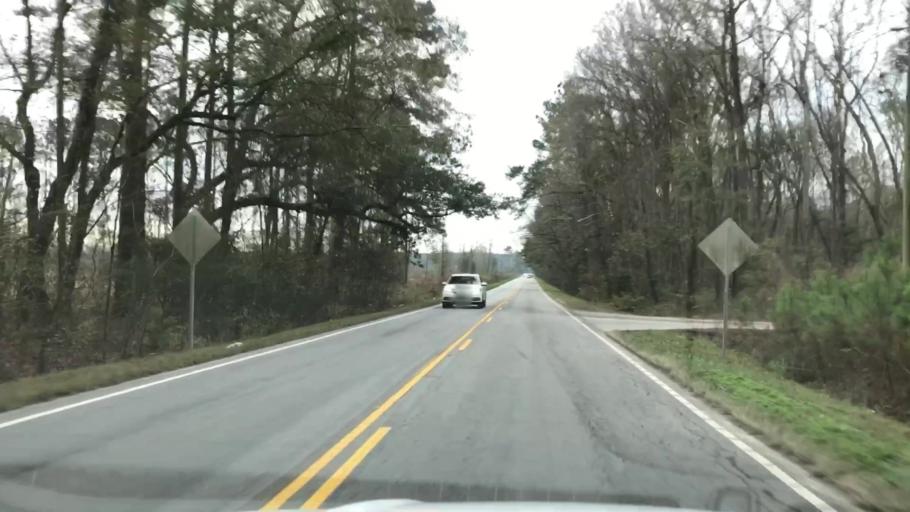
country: US
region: South Carolina
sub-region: Jasper County
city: Ridgeland
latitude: 32.4264
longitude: -80.8969
